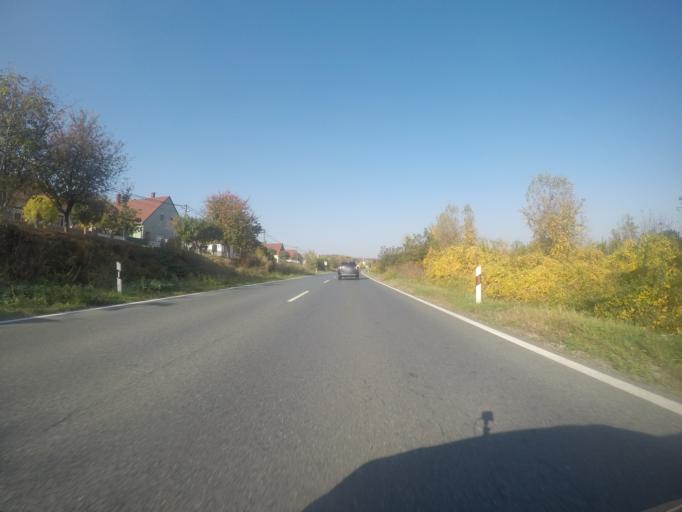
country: HU
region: Tolna
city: Paks
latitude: 46.6699
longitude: 18.8803
